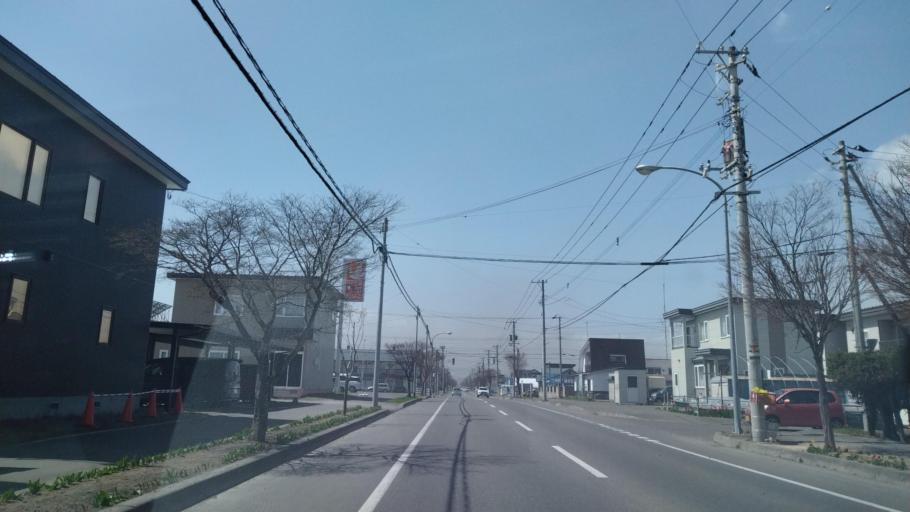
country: JP
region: Hokkaido
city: Obihiro
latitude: 42.9401
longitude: 143.1769
